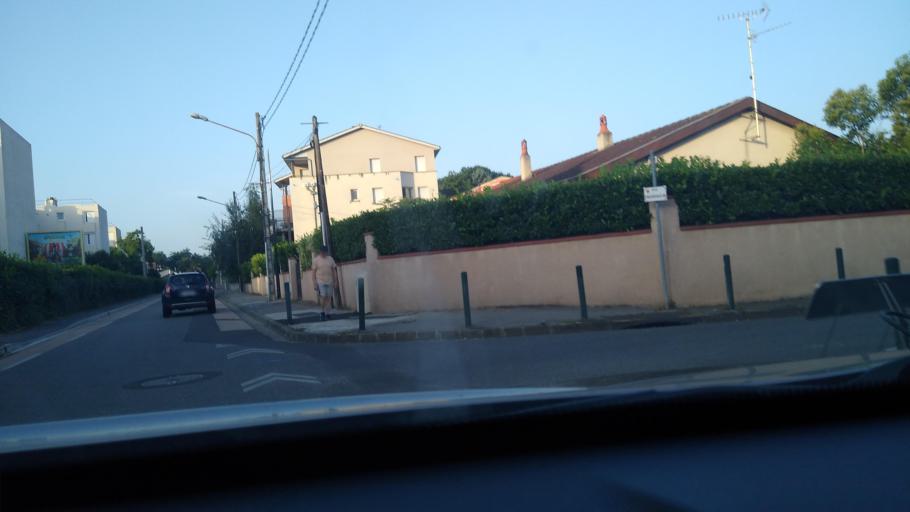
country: FR
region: Midi-Pyrenees
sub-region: Departement de la Haute-Garonne
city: Toulouse
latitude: 43.6271
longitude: 1.4562
